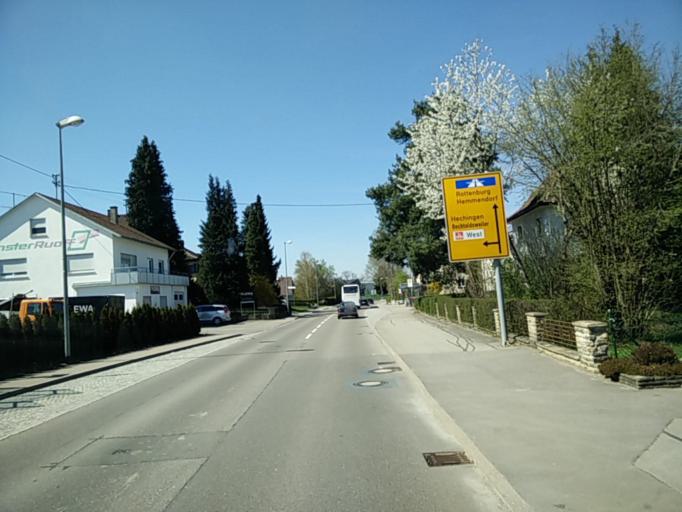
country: DE
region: Baden-Wuerttemberg
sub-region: Tuebingen Region
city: Bodelshausen
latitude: 48.3878
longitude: 8.9788
